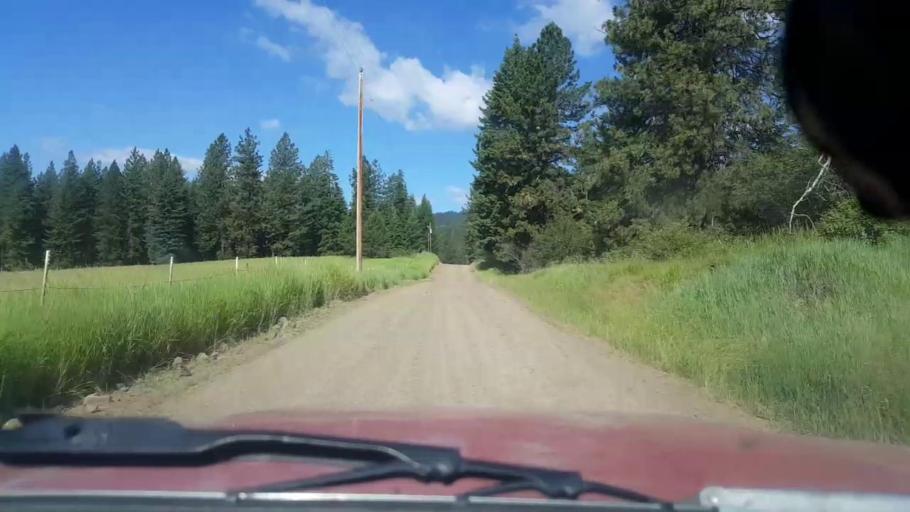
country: US
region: Washington
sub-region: Garfield County
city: Pomeroy
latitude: 46.0369
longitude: -117.4292
